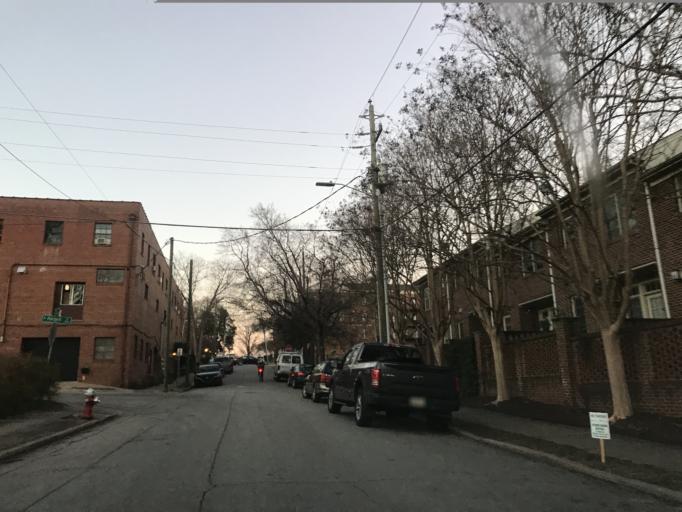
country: US
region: North Carolina
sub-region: Wake County
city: West Raleigh
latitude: 35.7791
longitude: -78.6522
